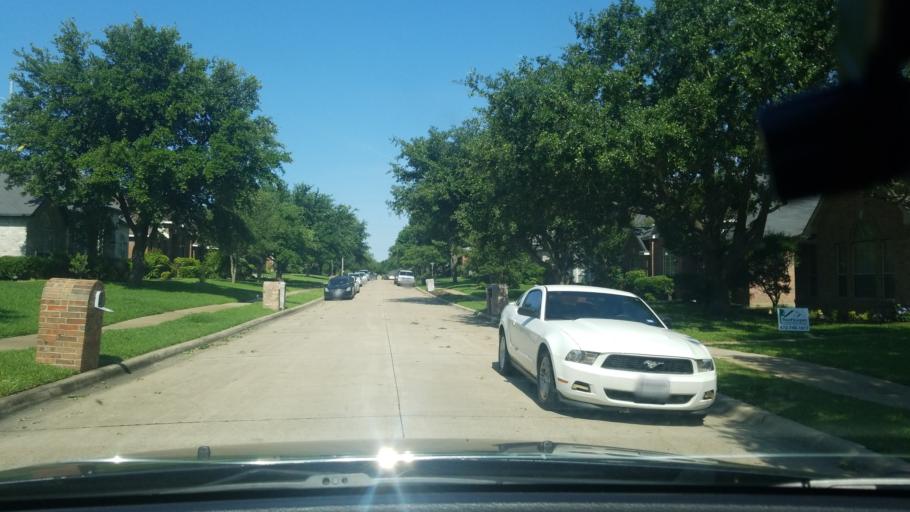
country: US
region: Texas
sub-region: Dallas County
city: Mesquite
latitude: 32.7759
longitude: -96.5842
